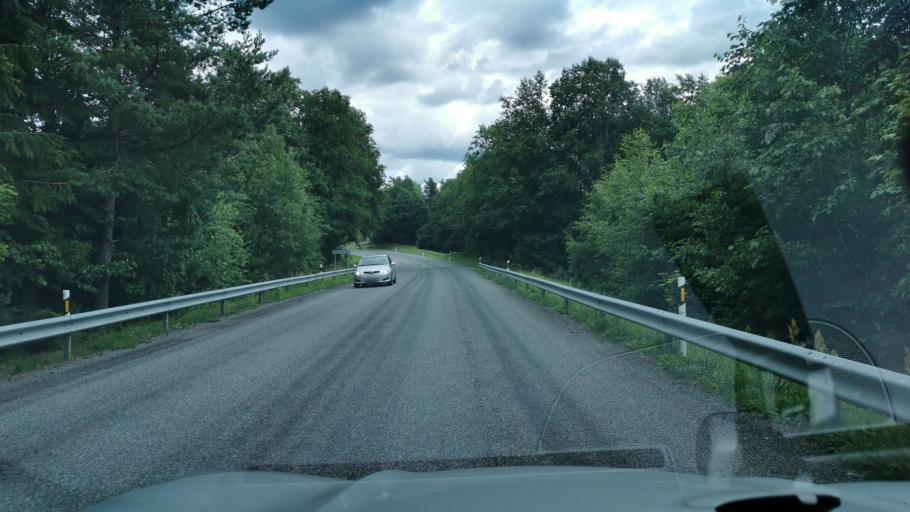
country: EE
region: Harju
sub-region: Anija vald
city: Kehra
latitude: 59.2190
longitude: 25.4503
